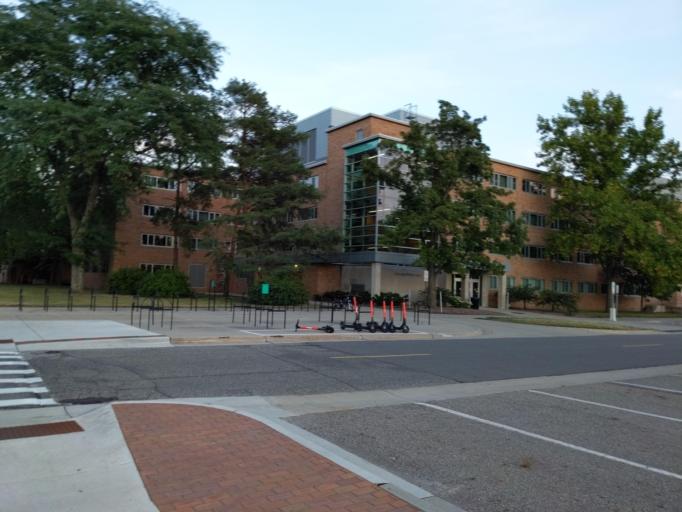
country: US
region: Michigan
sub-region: Ingham County
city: East Lansing
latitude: 42.7314
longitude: -84.4979
